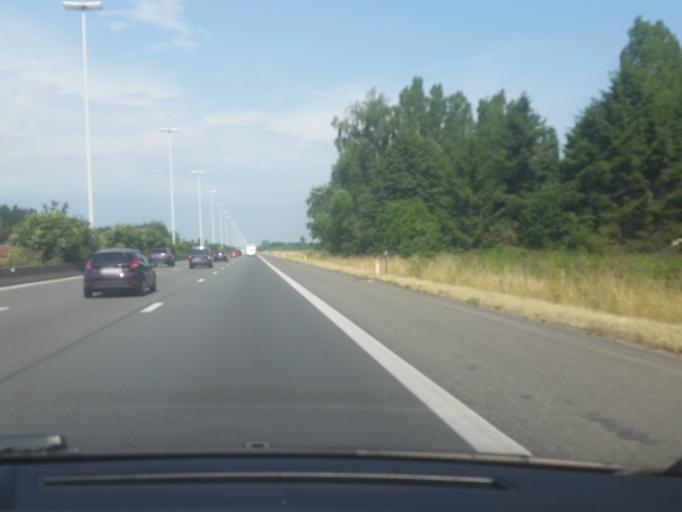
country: BE
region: Flanders
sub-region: Provincie West-Vlaanderen
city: Beernem
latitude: 51.1288
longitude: 3.2970
